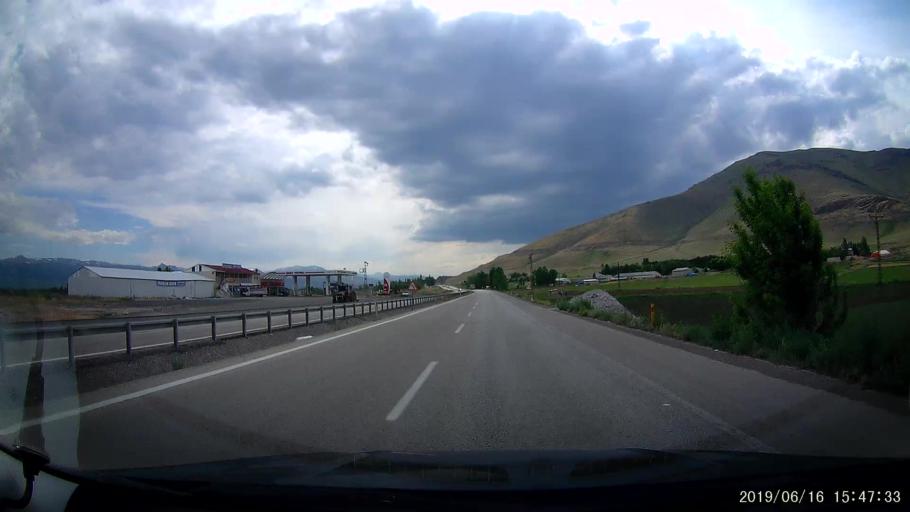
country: TR
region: Erzurum
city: Pasinler
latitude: 39.9881
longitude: 41.7183
